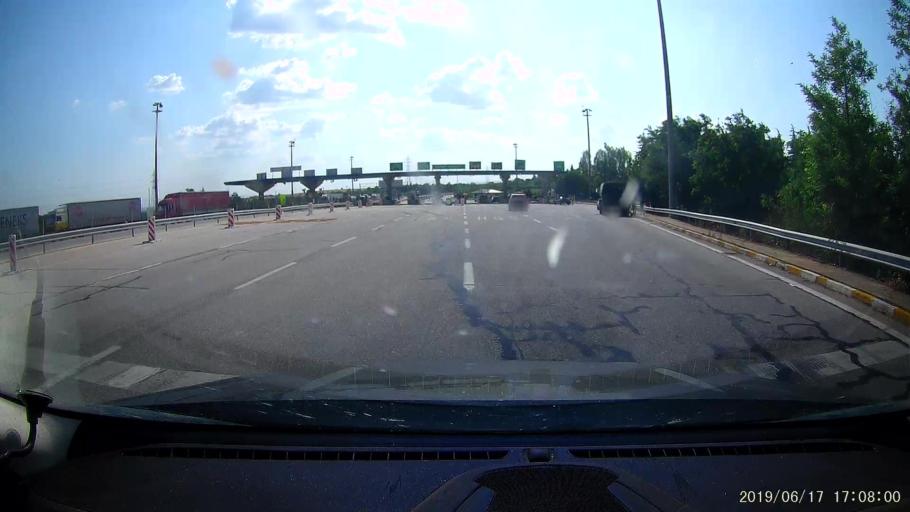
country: TR
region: Edirne
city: Edirne
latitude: 41.6610
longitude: 26.6315
